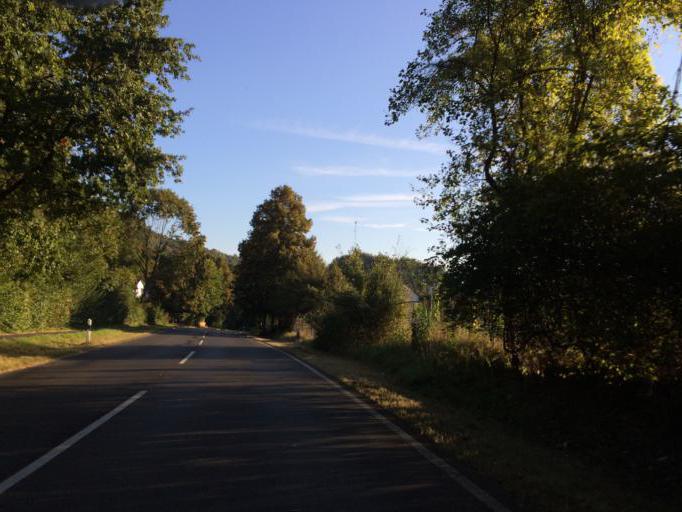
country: DE
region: North Rhine-Westphalia
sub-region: Regierungsbezirk Koln
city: Wachtberg
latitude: 50.6572
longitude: 7.1236
